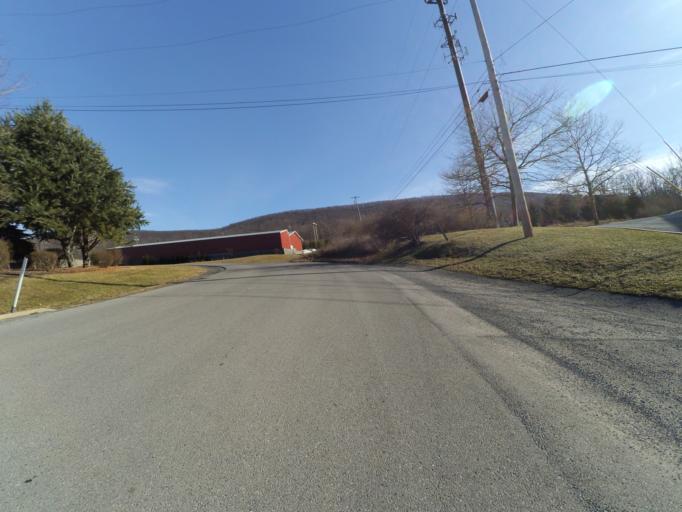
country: US
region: Pennsylvania
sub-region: Centre County
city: Lemont
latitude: 40.8249
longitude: -77.8015
